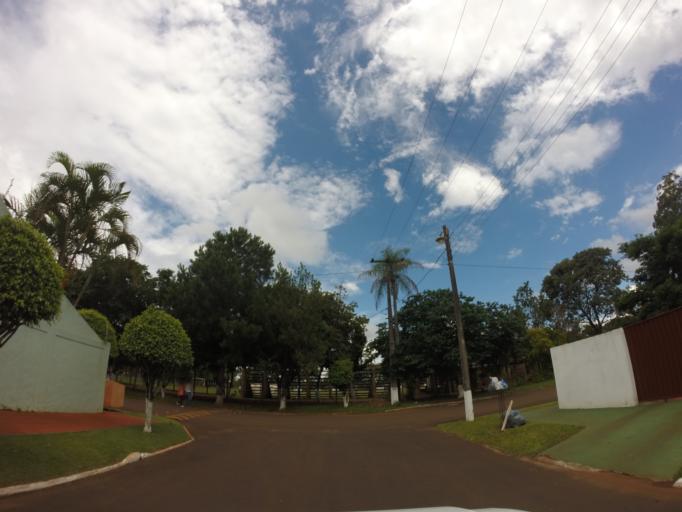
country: PY
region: Alto Parana
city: Ciudad del Este
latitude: -25.4159
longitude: -54.6252
